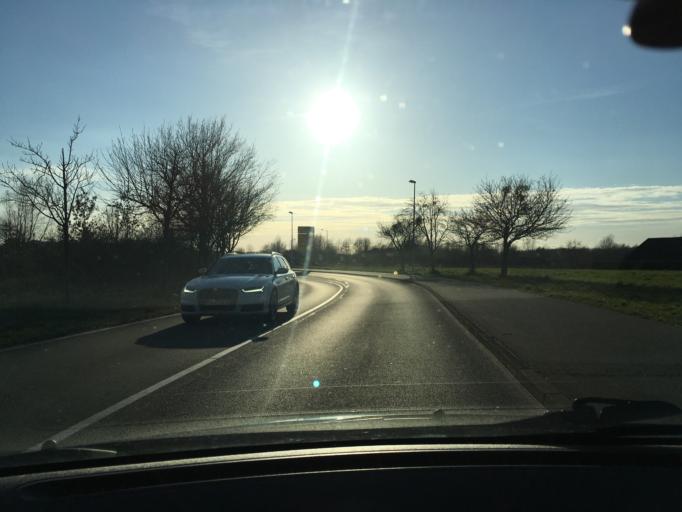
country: DE
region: Mecklenburg-Vorpommern
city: Feldstadt
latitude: 53.5936
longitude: 11.4061
